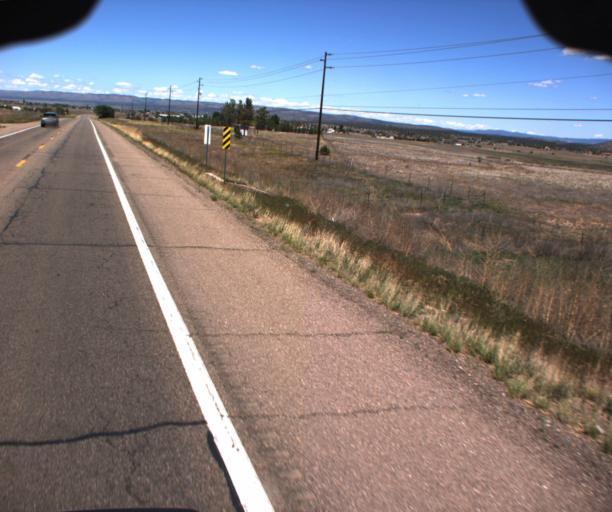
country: US
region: Arizona
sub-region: Yavapai County
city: Paulden
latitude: 34.8361
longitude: -112.4619
